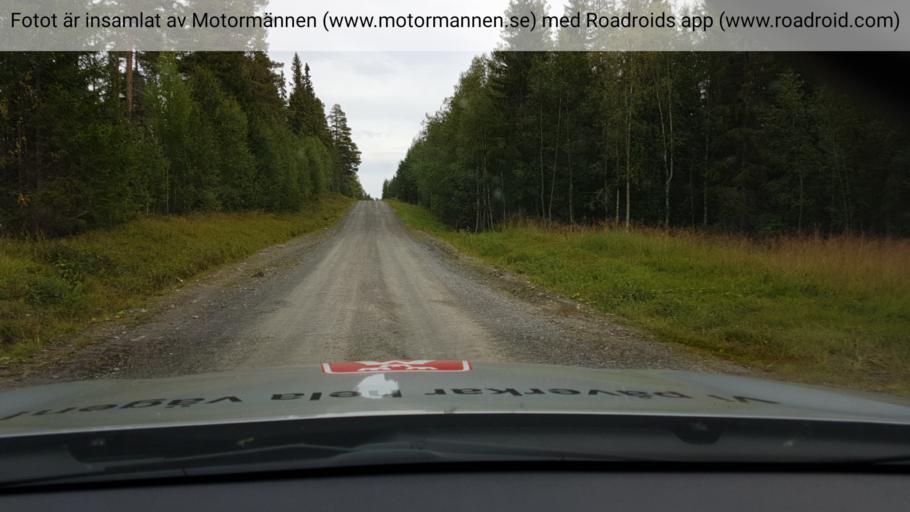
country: SE
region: Jaemtland
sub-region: Krokoms Kommun
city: Valla
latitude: 63.5833
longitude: 13.9633
